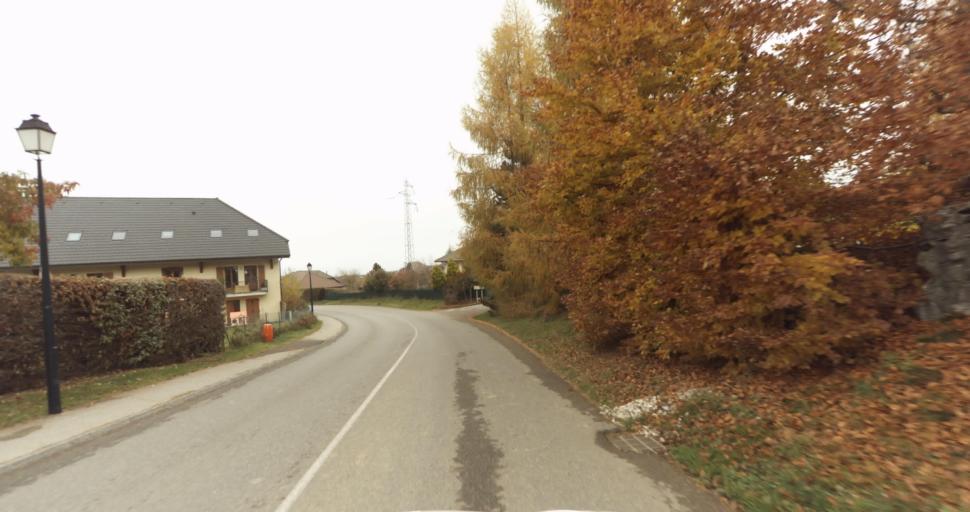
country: FR
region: Rhone-Alpes
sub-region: Departement de la Haute-Savoie
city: Viuz-la-Chiesaz
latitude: 45.8424
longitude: 6.0849
